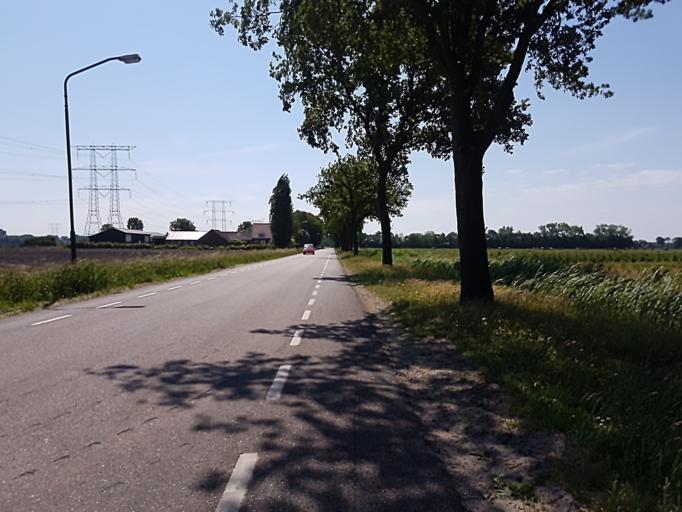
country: NL
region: North Brabant
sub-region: Gemeente Dongen
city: Dongen
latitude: 51.6313
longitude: 4.9958
